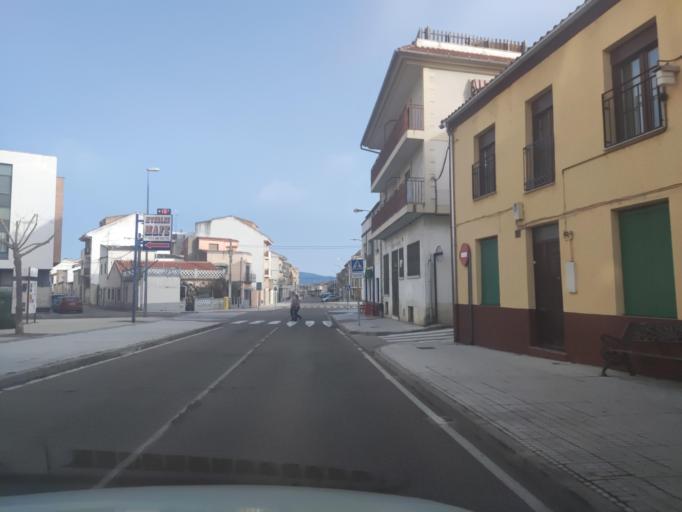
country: ES
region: Castille and Leon
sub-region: Provincia de Salamanca
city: Ciudad Rodrigo
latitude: 40.5970
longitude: -6.5263
